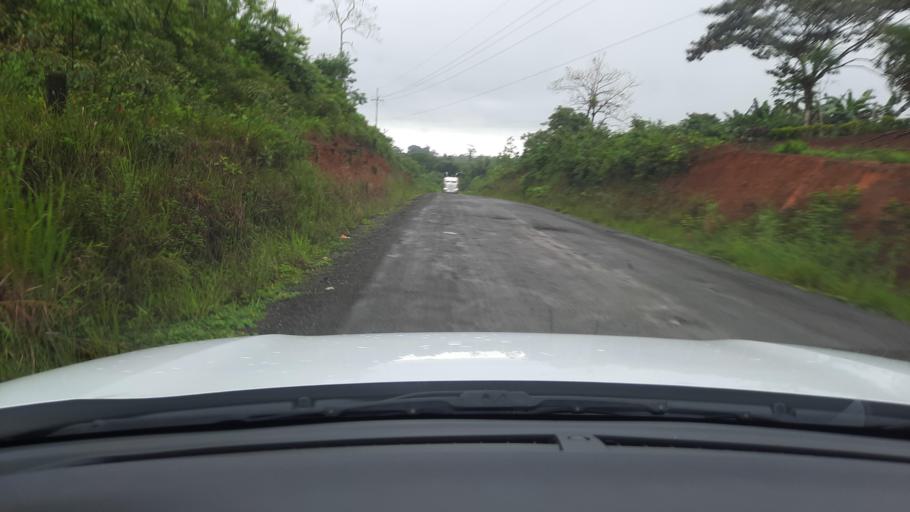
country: CR
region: Alajuela
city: San Jose
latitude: 11.0138
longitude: -85.3373
